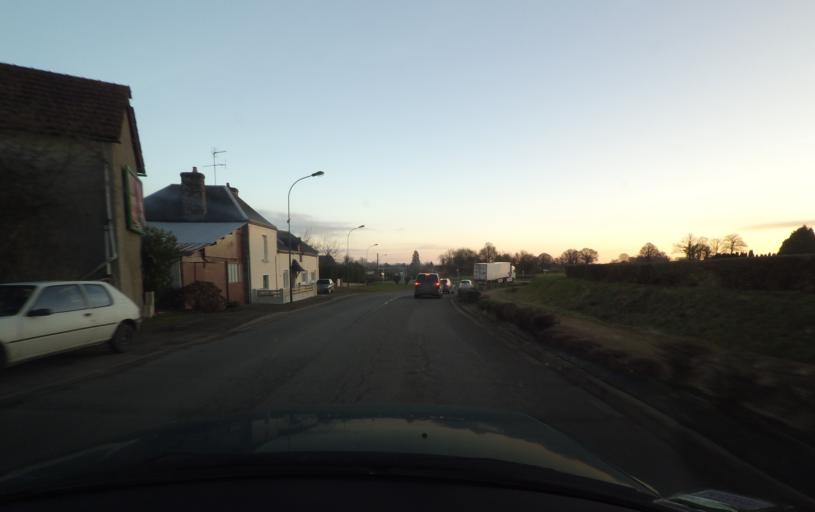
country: FR
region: Pays de la Loire
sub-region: Departement de la Mayenne
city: Bais
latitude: 48.2919
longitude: -0.3603
